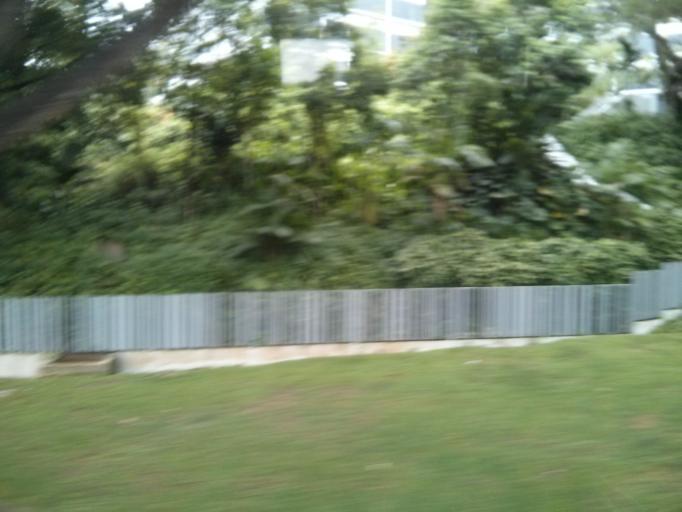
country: SG
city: Singapore
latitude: 1.2835
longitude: 103.8015
